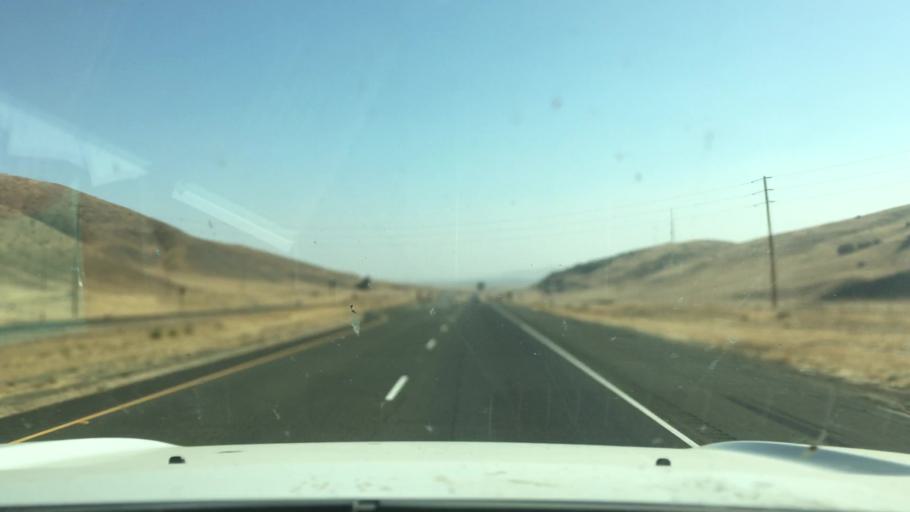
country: US
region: California
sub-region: San Luis Obispo County
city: Shandon
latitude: 35.7237
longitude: -120.1883
